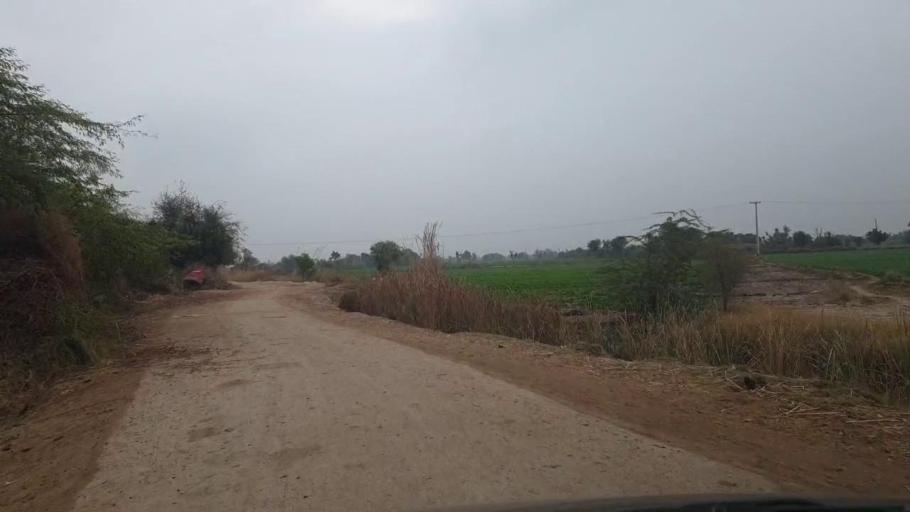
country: PK
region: Sindh
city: Tando Adam
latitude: 25.8498
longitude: 68.7007
